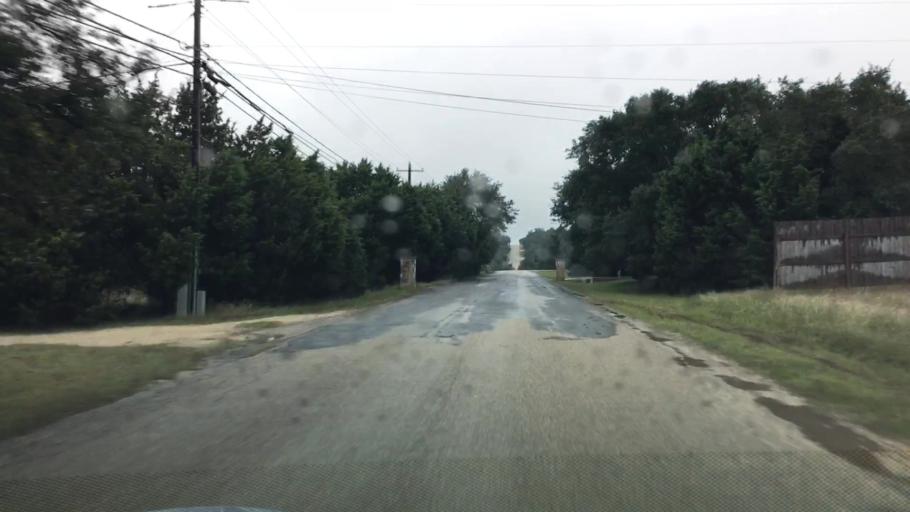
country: US
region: Texas
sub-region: Hays County
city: Dripping Springs
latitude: 30.1961
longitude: -98.0195
